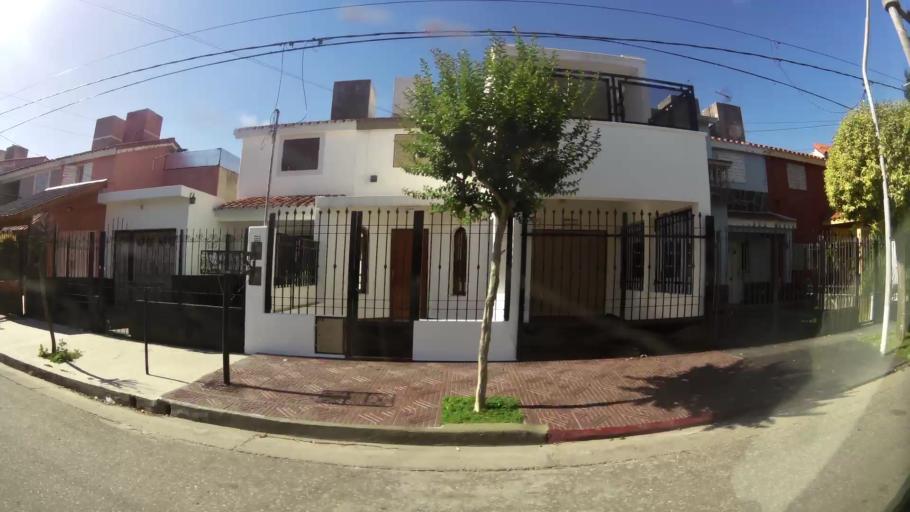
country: AR
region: Cordoba
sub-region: Departamento de Capital
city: Cordoba
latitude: -31.3583
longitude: -64.1820
